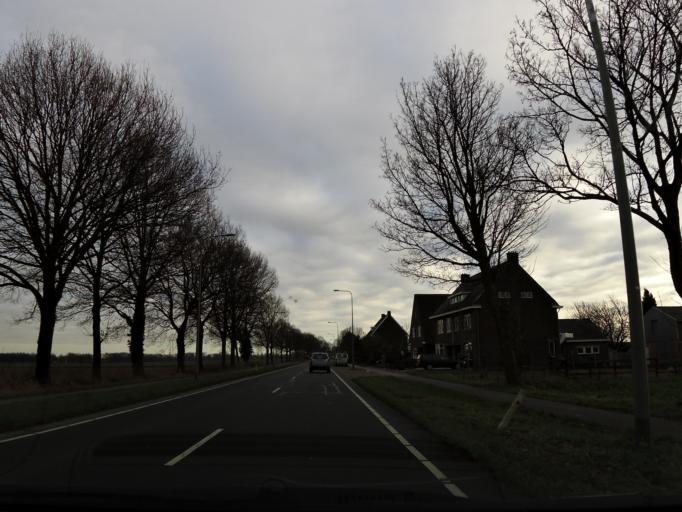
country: NL
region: Limburg
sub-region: Gemeente Schinnen
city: Oirsbeek
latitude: 50.9415
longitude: 5.9026
